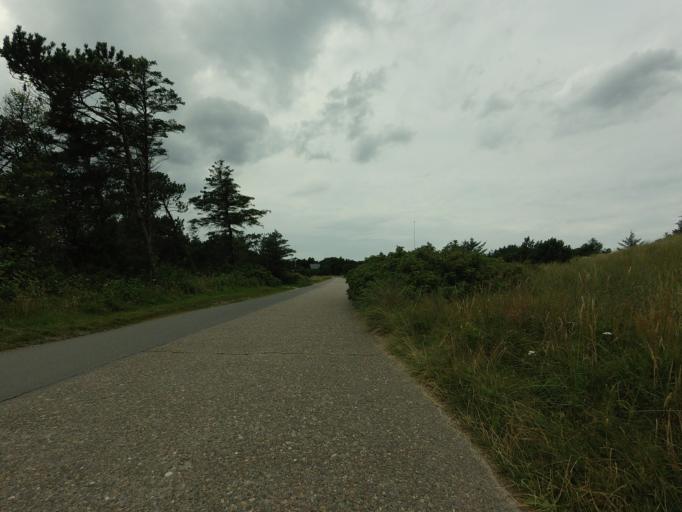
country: DK
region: North Denmark
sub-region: Jammerbugt Kommune
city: Pandrup
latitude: 57.3111
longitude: 9.6583
